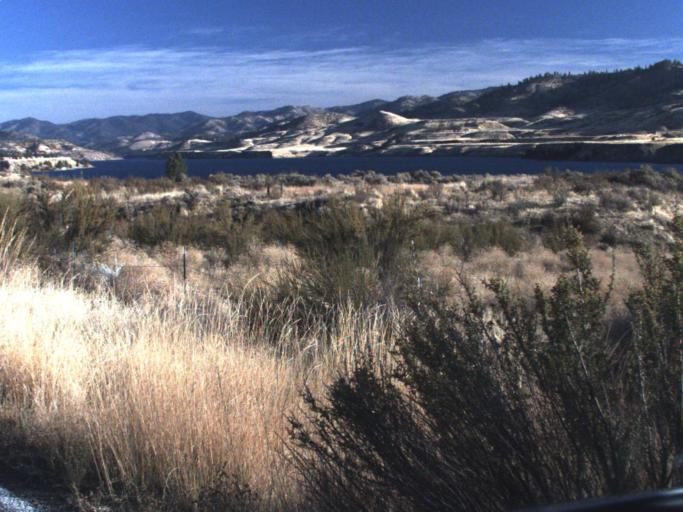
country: US
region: Washington
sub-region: Okanogan County
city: Coulee Dam
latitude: 47.9623
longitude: -118.7004
